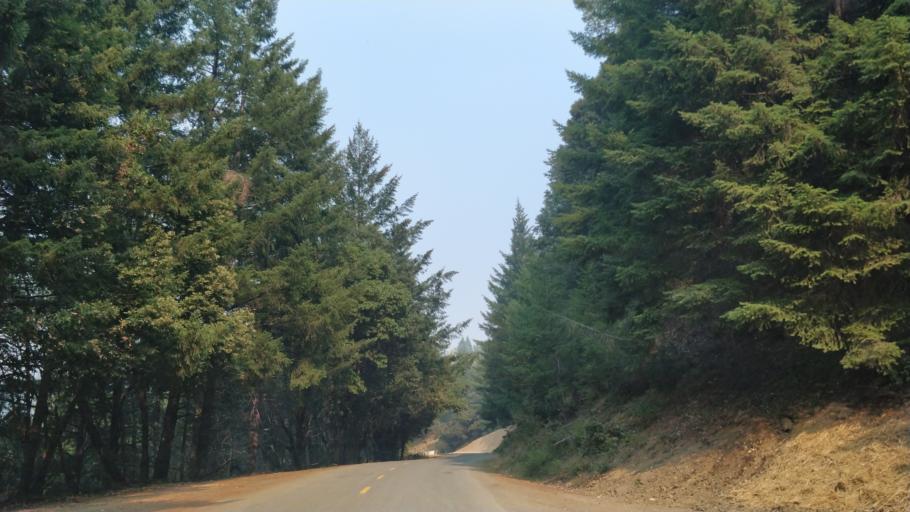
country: US
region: California
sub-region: Humboldt County
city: Rio Dell
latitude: 40.2613
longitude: -124.0979
